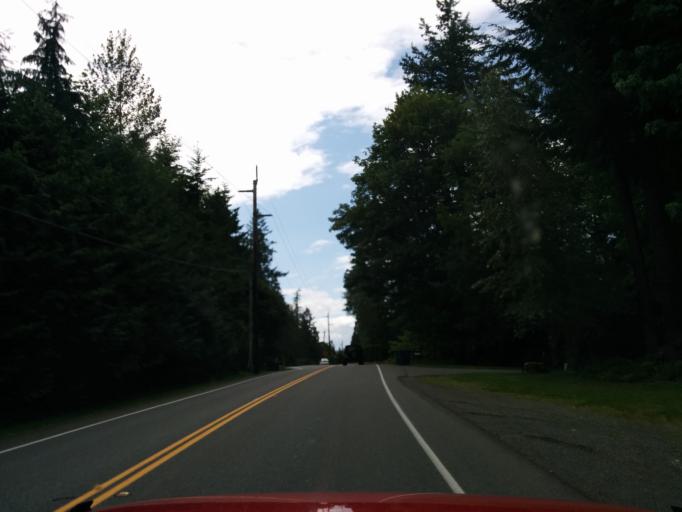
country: US
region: Washington
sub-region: King County
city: Union Hill-Novelty Hill
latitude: 47.6621
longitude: -122.0126
